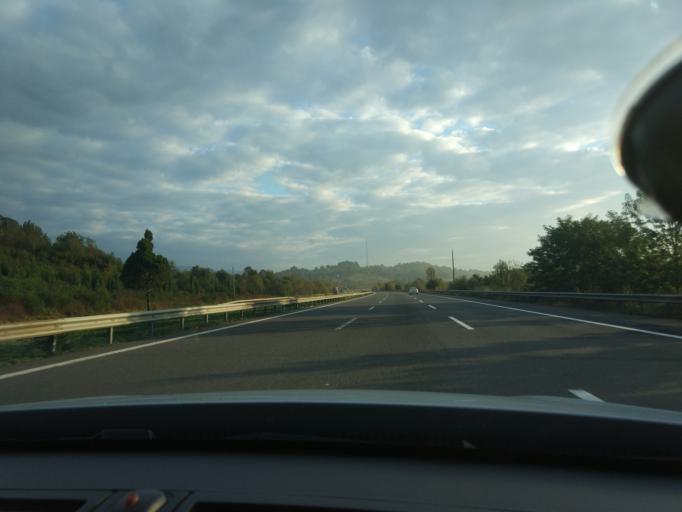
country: TR
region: Sakarya
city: Hendek
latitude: 40.7627
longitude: 30.7560
